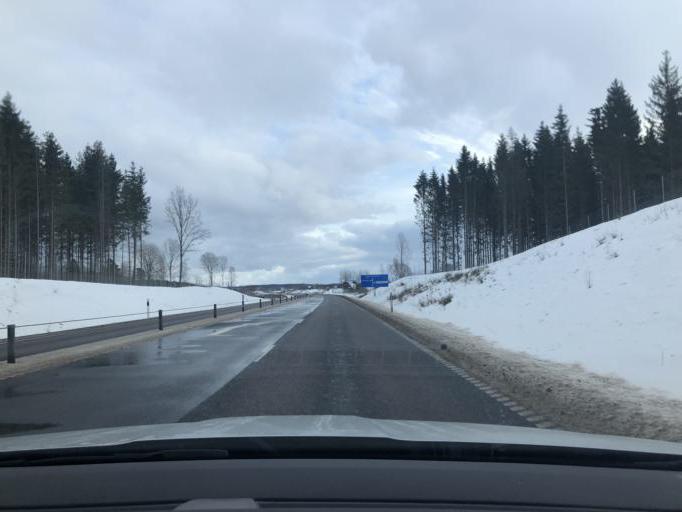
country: SE
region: OEstergoetland
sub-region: Motala Kommun
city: Borensberg
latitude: 58.5864
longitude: 15.1949
